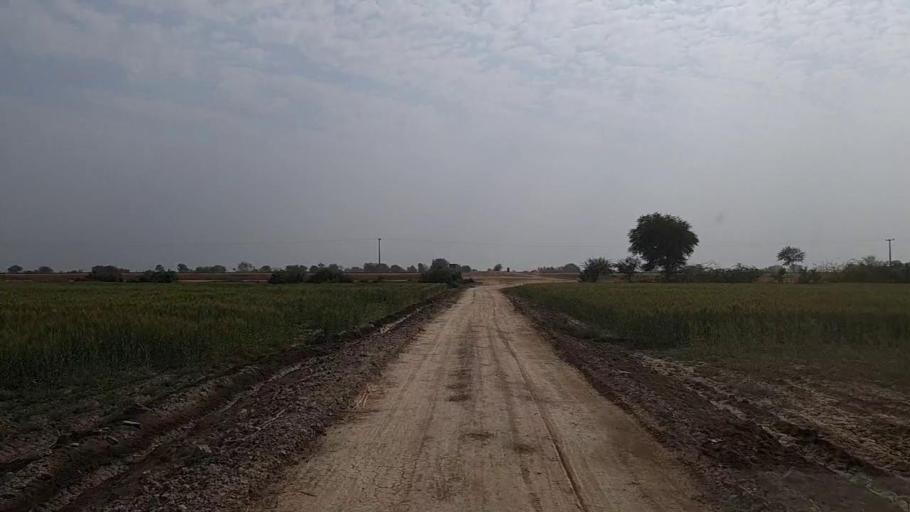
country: PK
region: Sindh
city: Mirwah Gorchani
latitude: 25.3987
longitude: 69.1018
